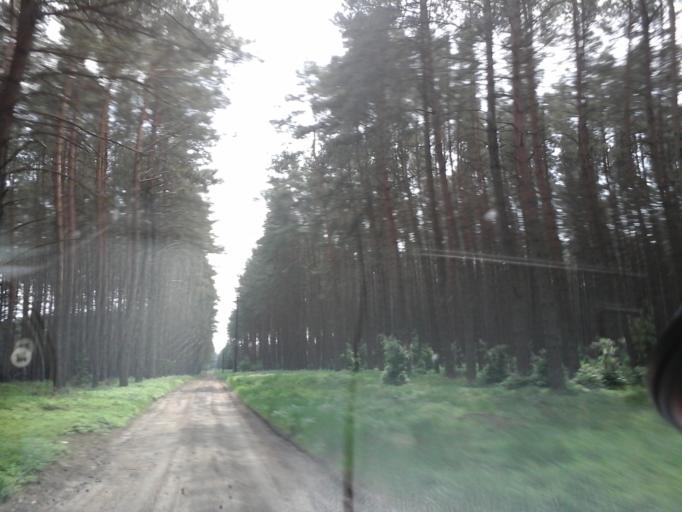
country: PL
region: West Pomeranian Voivodeship
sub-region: Powiat choszczenski
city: Drawno
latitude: 53.1242
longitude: 15.7988
